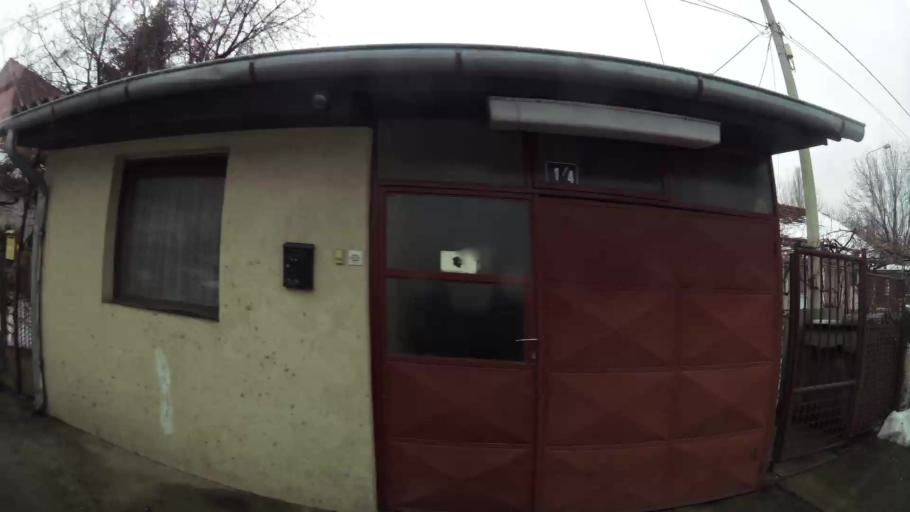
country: RS
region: Central Serbia
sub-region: Belgrade
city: Zemun
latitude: 44.8341
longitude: 20.3764
